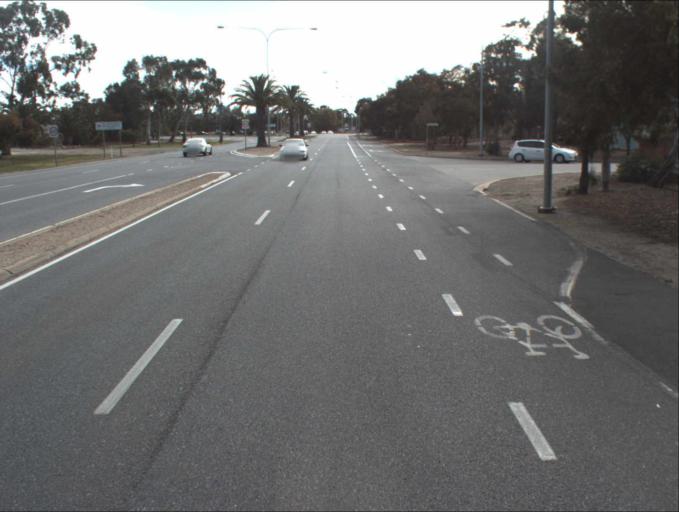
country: AU
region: South Australia
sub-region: Charles Sturt
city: West Lakes Shore
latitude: -34.8552
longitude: 138.5024
